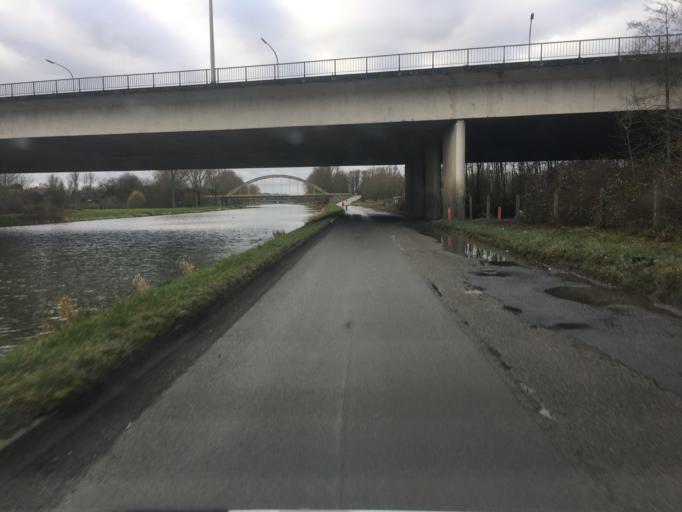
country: BE
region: Wallonia
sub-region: Province du Hainaut
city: Manage
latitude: 50.5116
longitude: 4.2121
